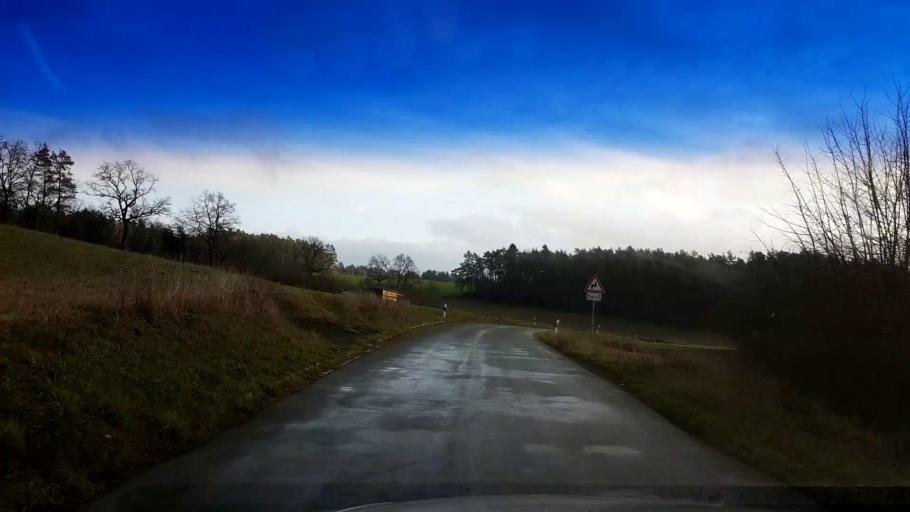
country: DE
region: Bavaria
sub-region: Upper Franconia
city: Poxdorf
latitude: 49.9315
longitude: 11.1262
